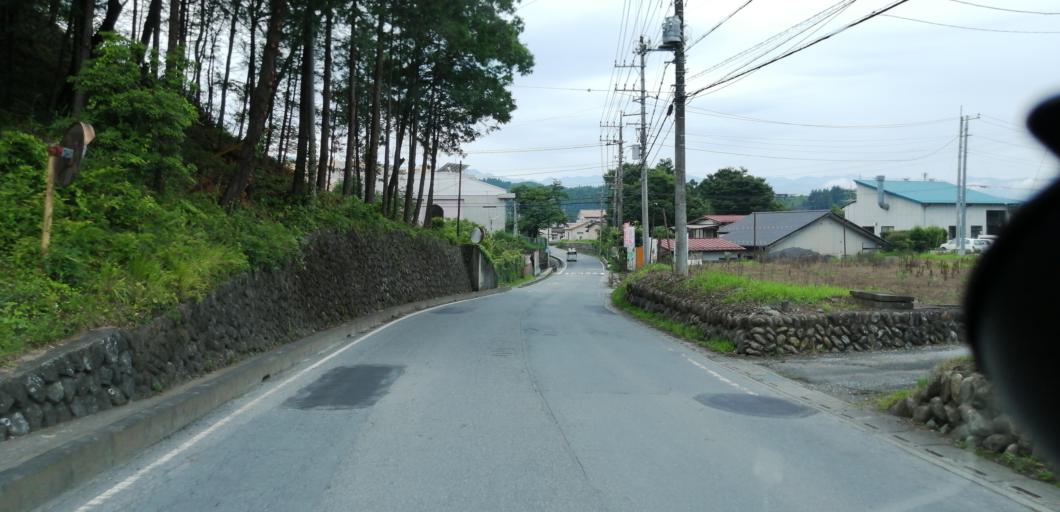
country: JP
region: Saitama
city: Chichibu
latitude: 36.0228
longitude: 139.1156
